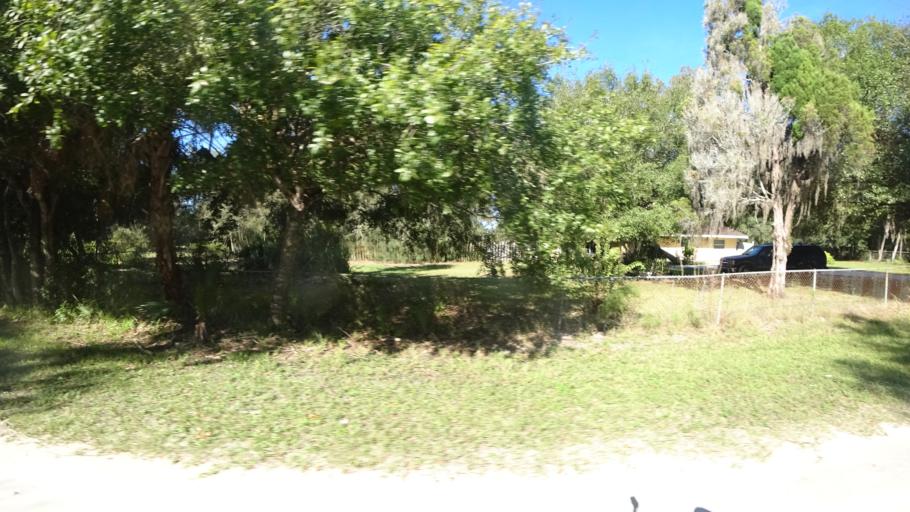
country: US
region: Florida
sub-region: Hillsborough County
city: Sun City Center
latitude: 27.6457
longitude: -82.3530
